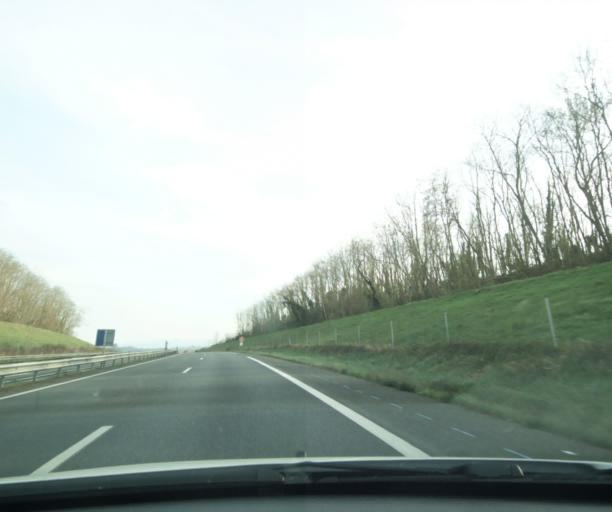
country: FR
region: Midi-Pyrenees
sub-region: Departement des Hautes-Pyrenees
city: Barbazan-Debat
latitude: 43.2026
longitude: 0.1478
